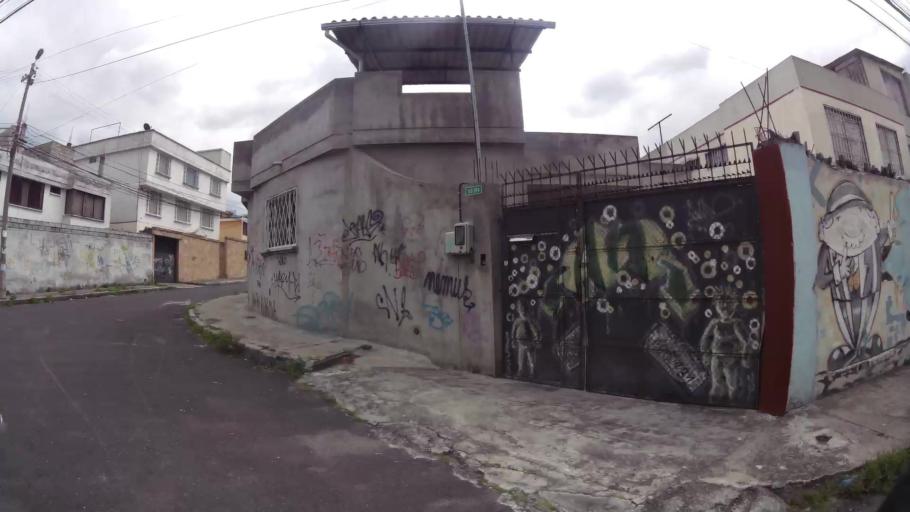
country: EC
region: Pichincha
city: Quito
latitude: -0.2468
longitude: -78.5282
